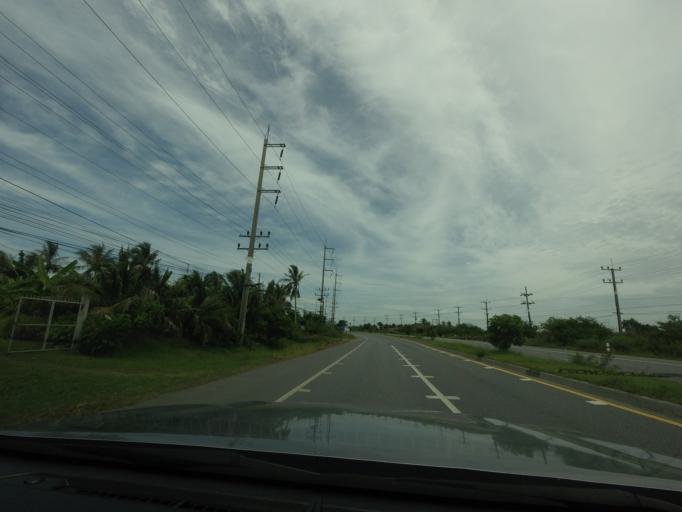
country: TH
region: Songkhla
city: Ranot
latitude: 7.7912
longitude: 100.3533
